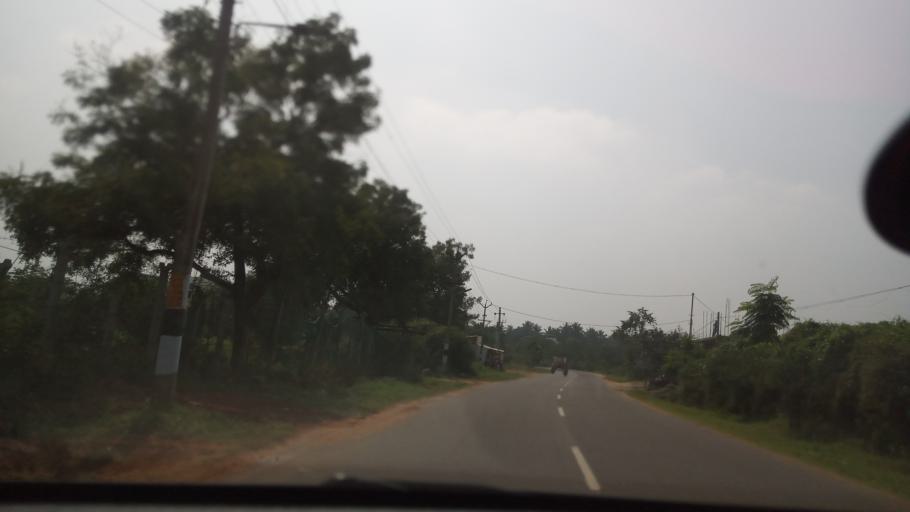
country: IN
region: Tamil Nadu
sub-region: Coimbatore
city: Perur
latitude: 11.0137
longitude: 76.8752
